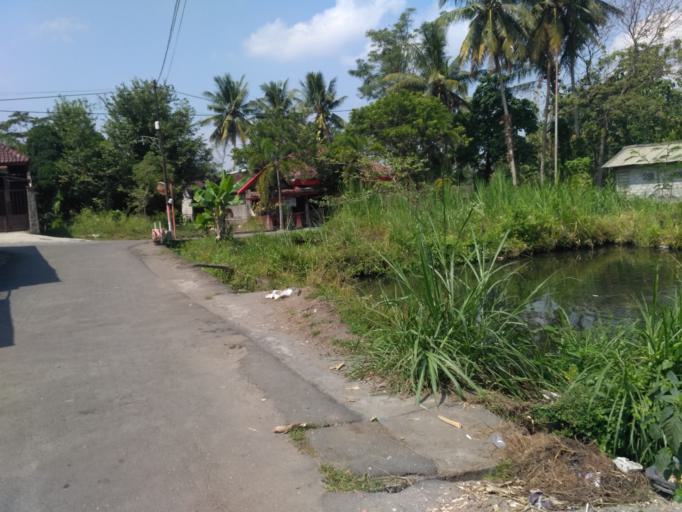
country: ID
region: Daerah Istimewa Yogyakarta
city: Melati
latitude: -7.7051
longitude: 110.4142
